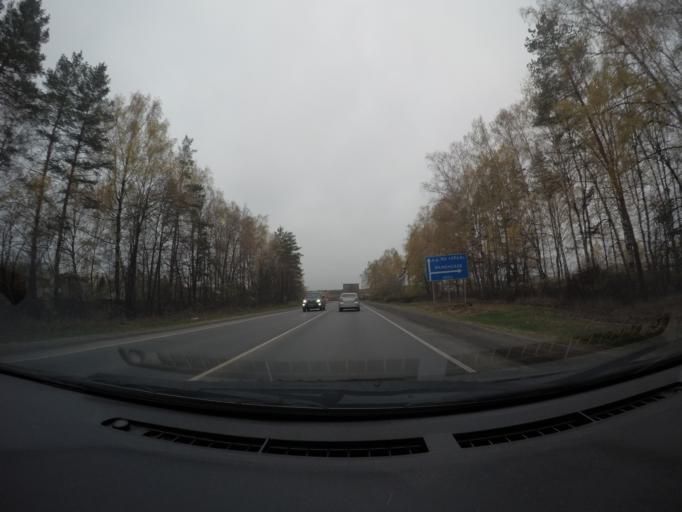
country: RU
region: Moskovskaya
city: Malyshevo
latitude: 55.4847
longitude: 38.3491
